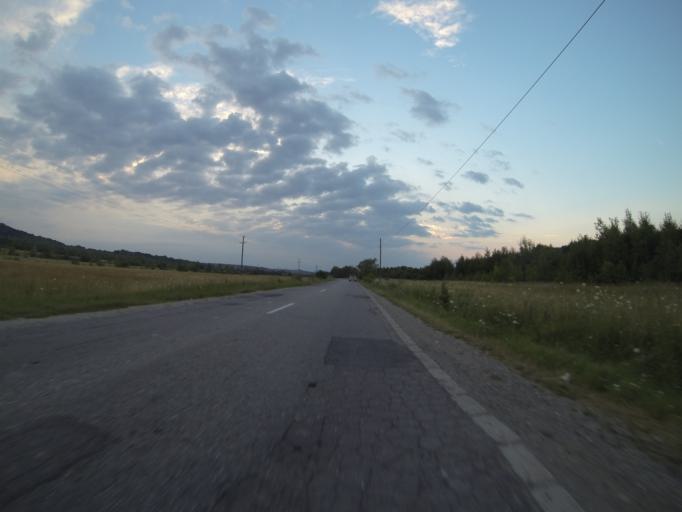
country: RO
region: Brasov
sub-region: Comuna Sinca Veche
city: Persani
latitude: 45.7415
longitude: 25.2149
